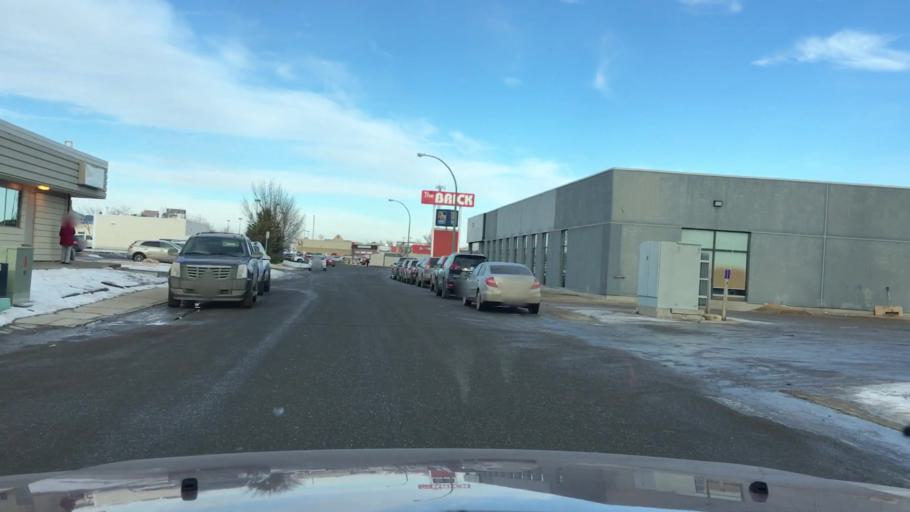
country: CA
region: Saskatchewan
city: Regina
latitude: 50.4795
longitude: -104.6166
